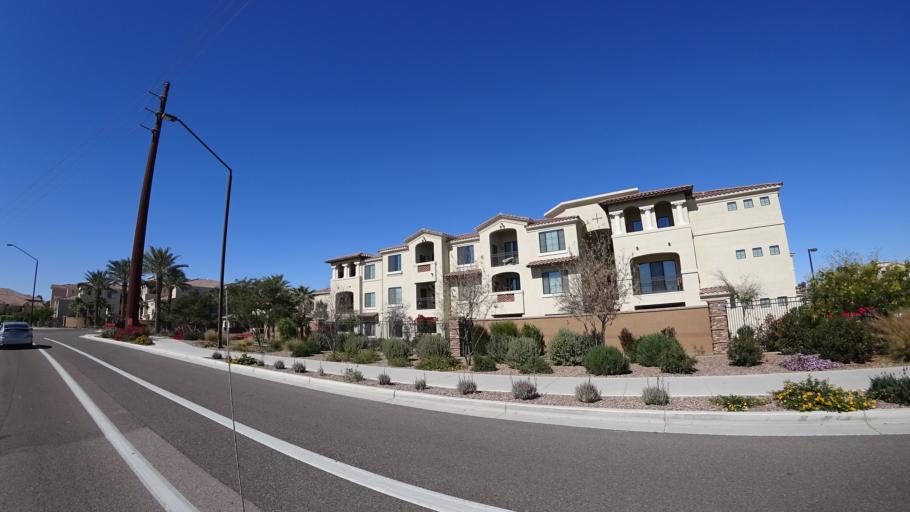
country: US
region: Arizona
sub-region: Maricopa County
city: Gilbert
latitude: 33.2956
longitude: -111.7570
